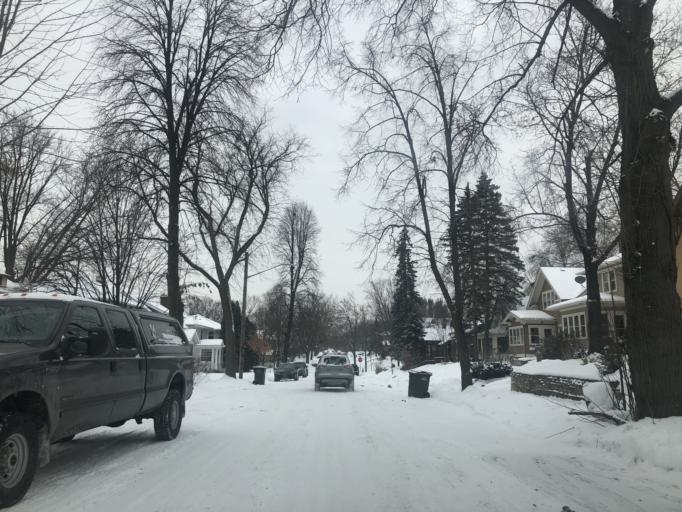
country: US
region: Minnesota
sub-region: Hennepin County
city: Richfield
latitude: 44.9242
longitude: -93.2922
